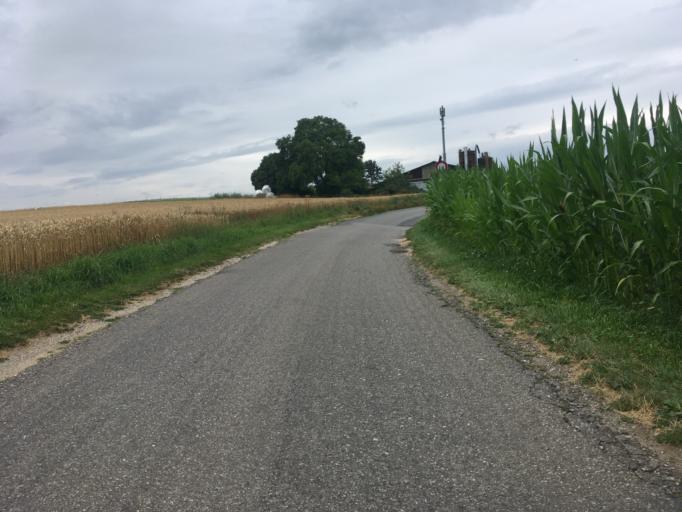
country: CH
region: Fribourg
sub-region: See District
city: Gurwolf
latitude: 46.9073
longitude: 7.0913
